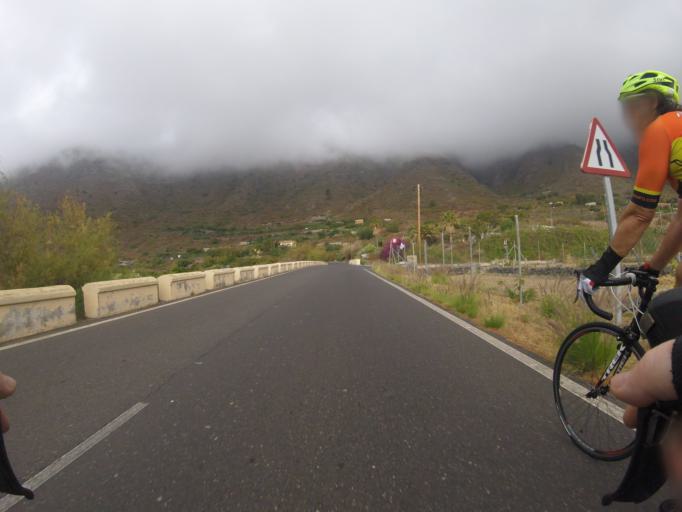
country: ES
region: Canary Islands
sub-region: Provincia de Santa Cruz de Tenerife
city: Guimar
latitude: 28.2993
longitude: -16.4177
